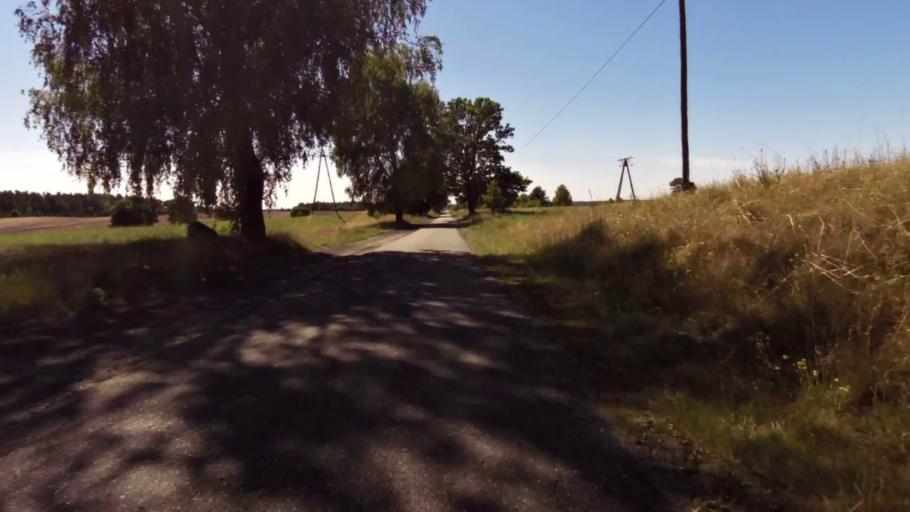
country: PL
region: West Pomeranian Voivodeship
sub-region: Powiat szczecinecki
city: Szczecinek
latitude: 53.7019
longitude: 16.6170
